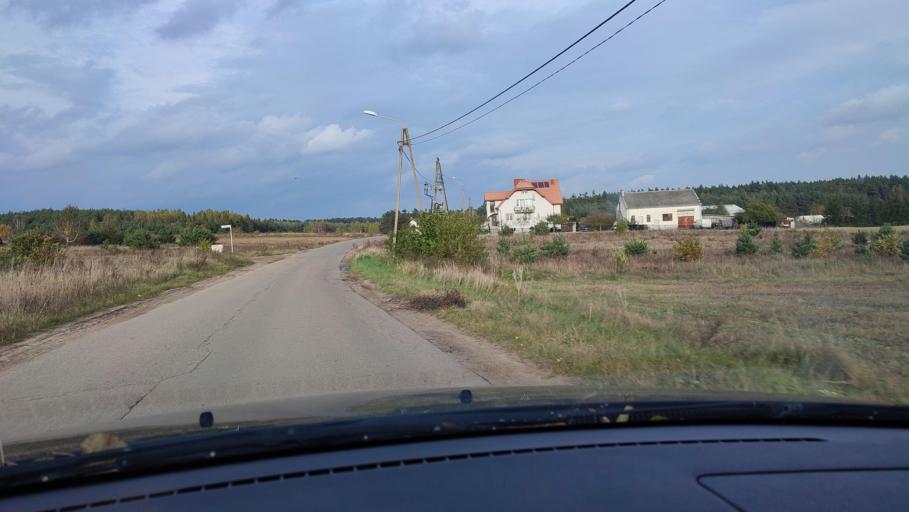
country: PL
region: Masovian Voivodeship
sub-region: Powiat mlawski
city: Mlawa
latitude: 53.1384
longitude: 20.3664
